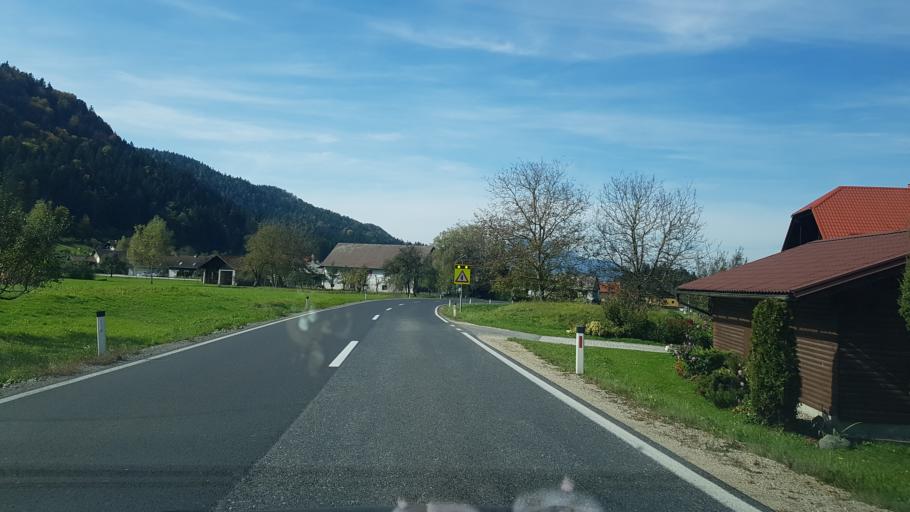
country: SI
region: Slovenj Gradec
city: Legen
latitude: 46.4466
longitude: 15.1767
